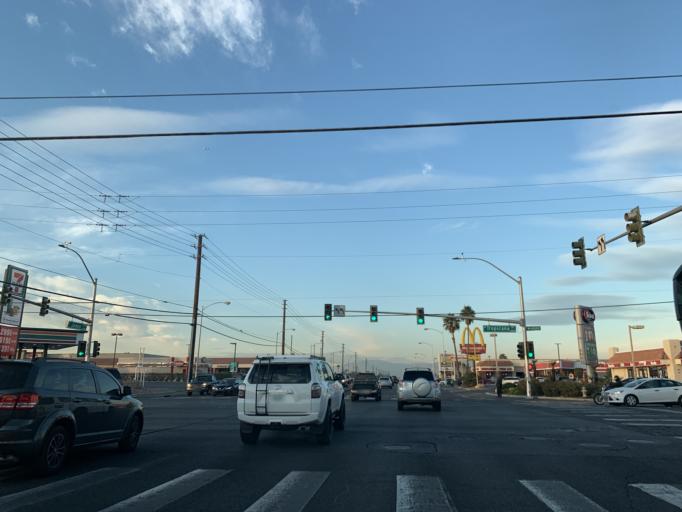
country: US
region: Nevada
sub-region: Clark County
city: Spring Valley
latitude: 36.0997
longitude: -115.2250
